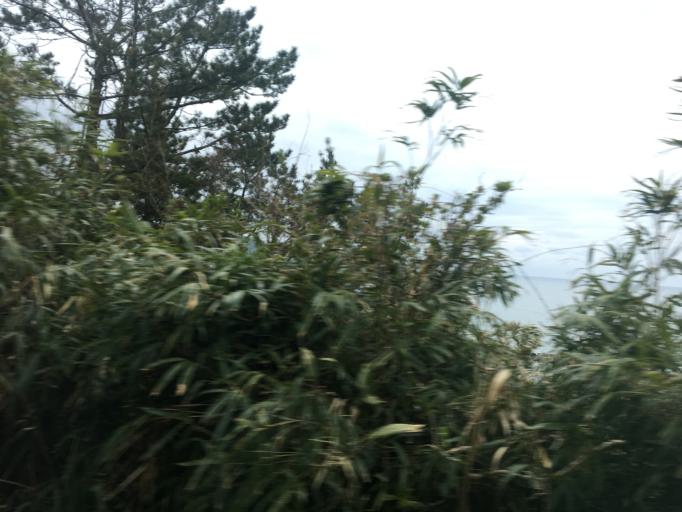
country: JP
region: Akita
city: Noshiromachi
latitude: 40.5872
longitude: 139.9076
